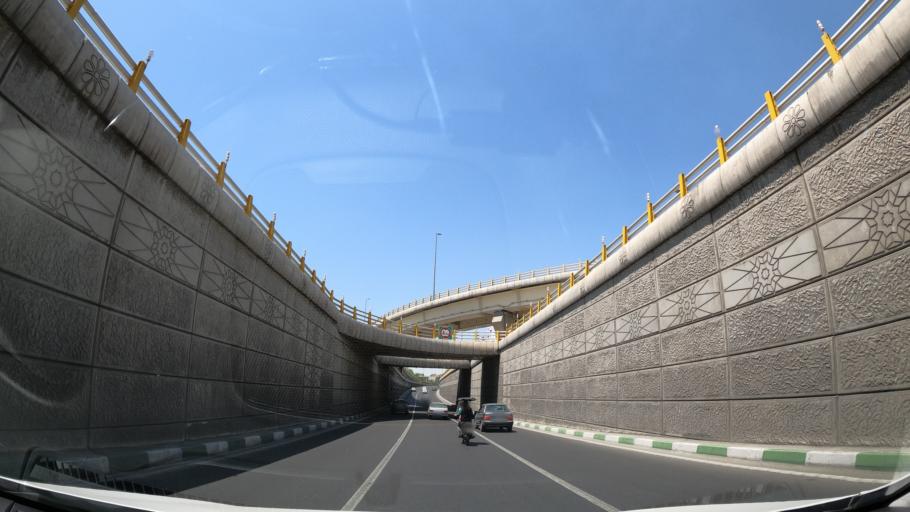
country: IR
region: Tehran
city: Tehran
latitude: 35.7245
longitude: 51.3954
